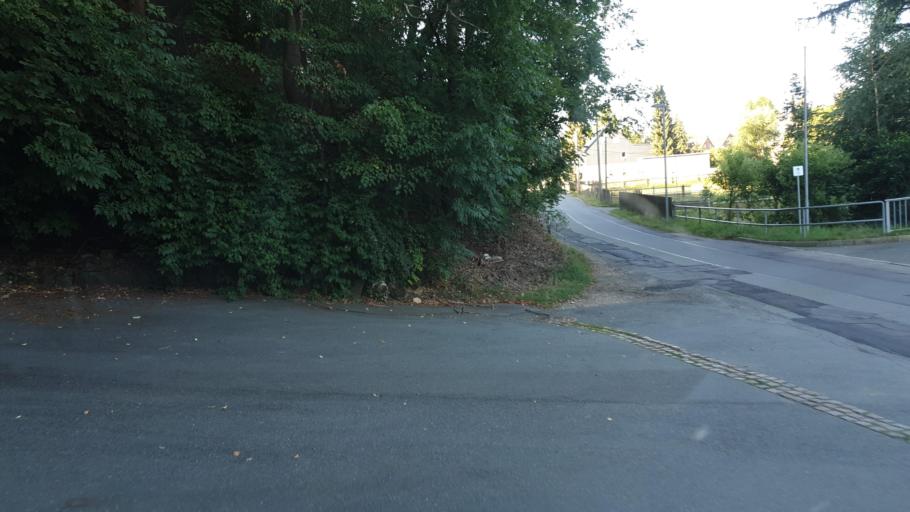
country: DE
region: Saxony
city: Lichtentanne
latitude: 50.6742
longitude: 12.4317
